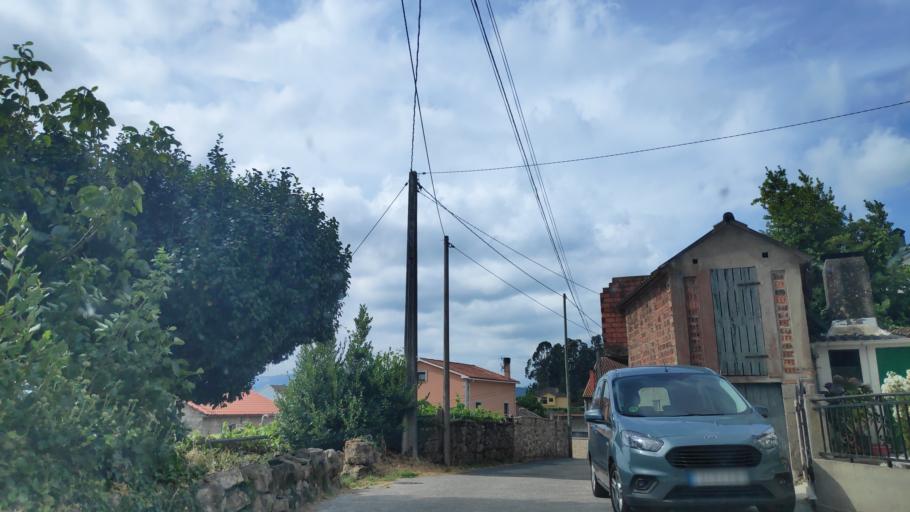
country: ES
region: Galicia
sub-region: Provincia da Coruna
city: Padron
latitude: 42.7294
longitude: -8.6735
